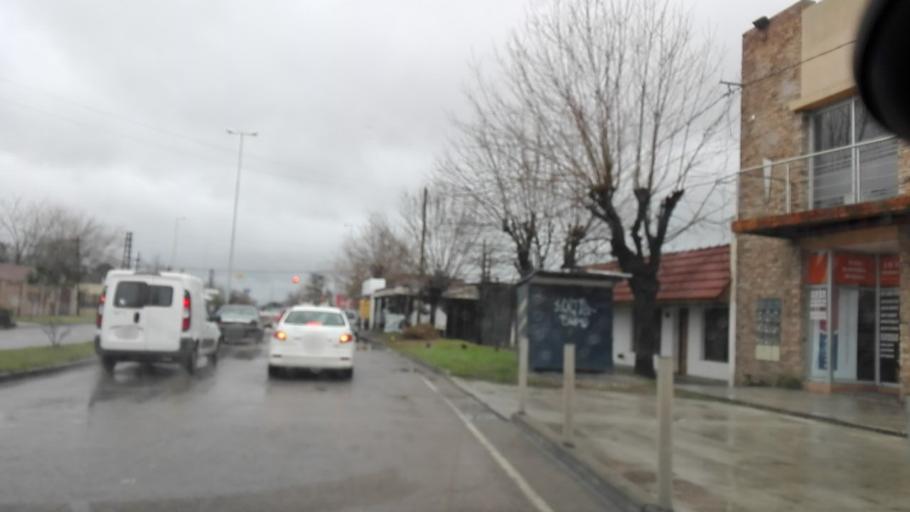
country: AR
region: Buenos Aires
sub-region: Partido de Brandsen
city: Brandsen
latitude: -35.1748
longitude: -58.2340
